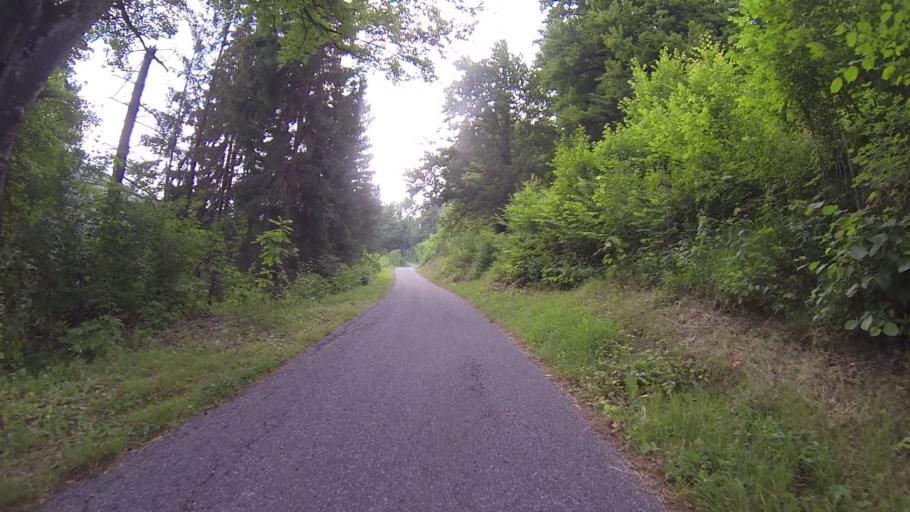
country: DE
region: Baden-Wuerttemberg
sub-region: Tuebingen Region
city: Blaubeuren
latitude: 48.4527
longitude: 9.8453
